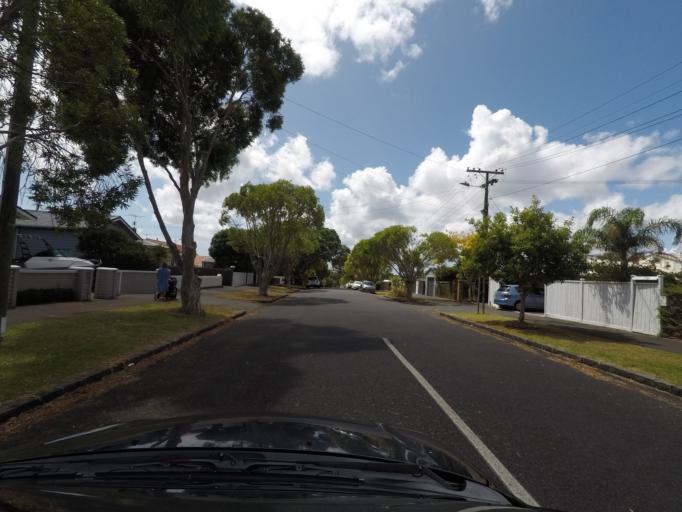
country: NZ
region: Auckland
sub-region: Auckland
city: Rosebank
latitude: -36.8590
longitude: 174.7059
